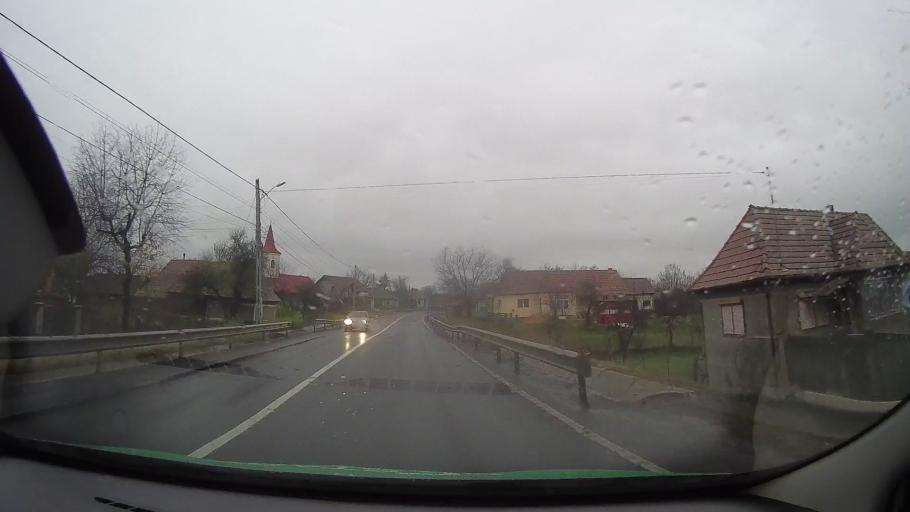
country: RO
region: Mures
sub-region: Comuna Brancovenesti
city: Brancovenesti
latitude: 46.8524
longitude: 24.7544
